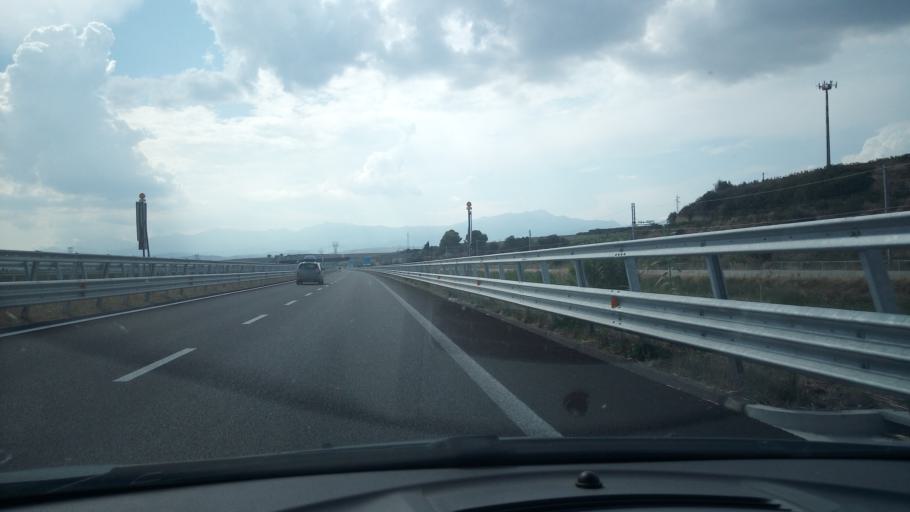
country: IT
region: Calabria
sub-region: Provincia di Cosenza
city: Doria
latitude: 39.7268
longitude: 16.3345
